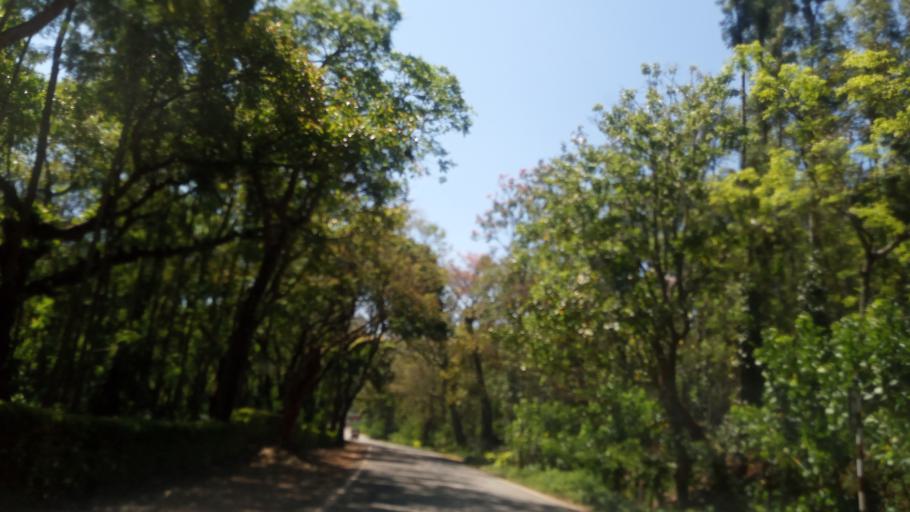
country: IN
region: Karnataka
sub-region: Chikmagalur
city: Chikmagalur
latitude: 13.4091
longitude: 75.7960
